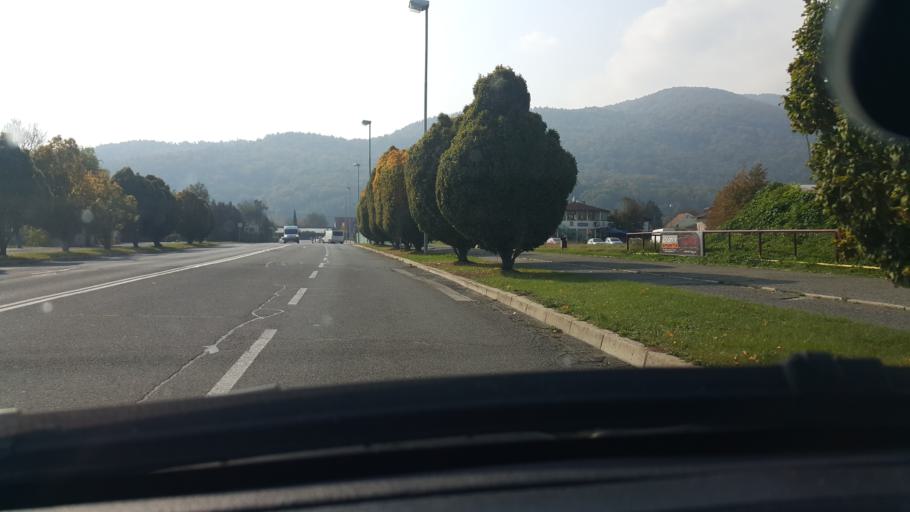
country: SI
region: Maribor
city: Razvanje
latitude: 46.5352
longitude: 15.6304
